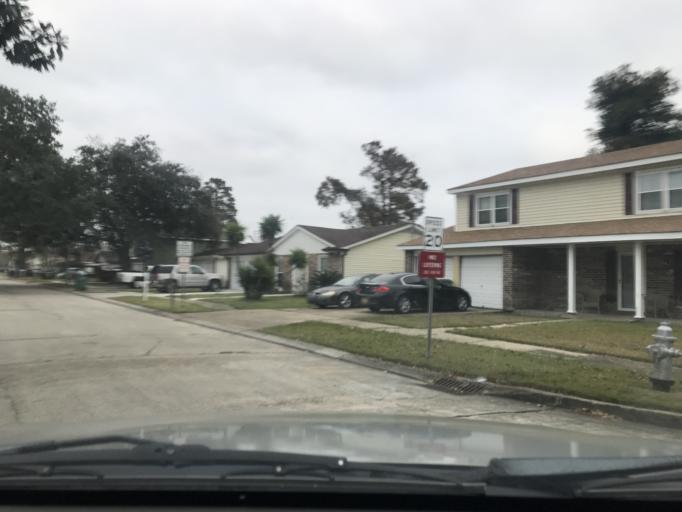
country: US
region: Louisiana
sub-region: Jefferson Parish
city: Woodmere
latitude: 29.8592
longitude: -90.0784
